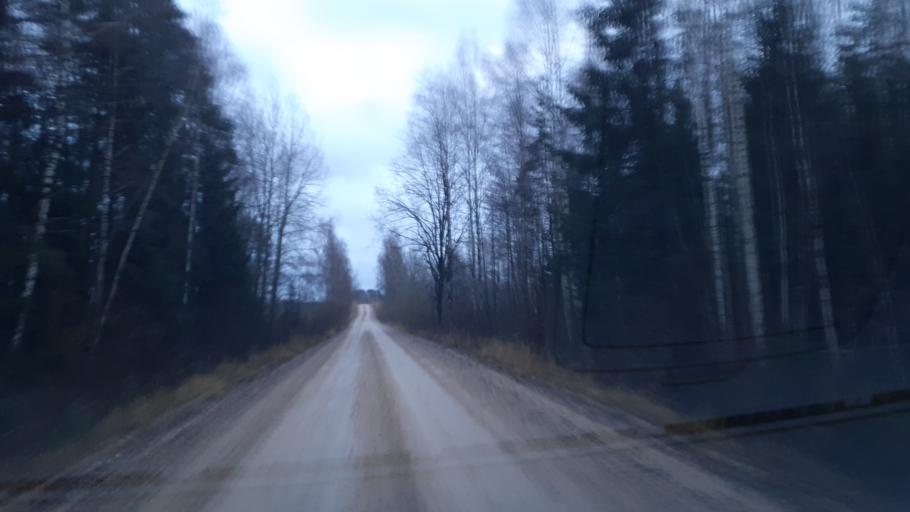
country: LV
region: Kuldigas Rajons
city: Kuldiga
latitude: 57.0503
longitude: 22.1260
